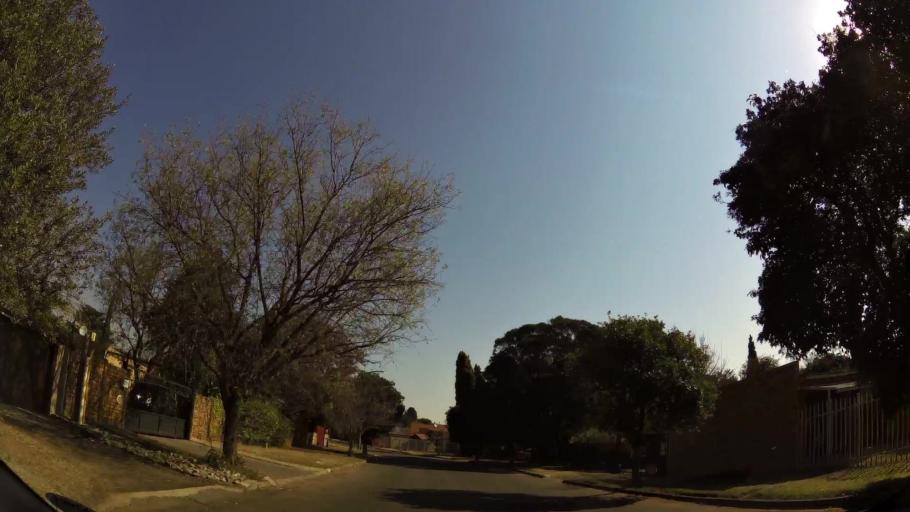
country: ZA
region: Gauteng
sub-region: Ekurhuleni Metropolitan Municipality
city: Boksburg
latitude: -26.1631
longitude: 28.2672
